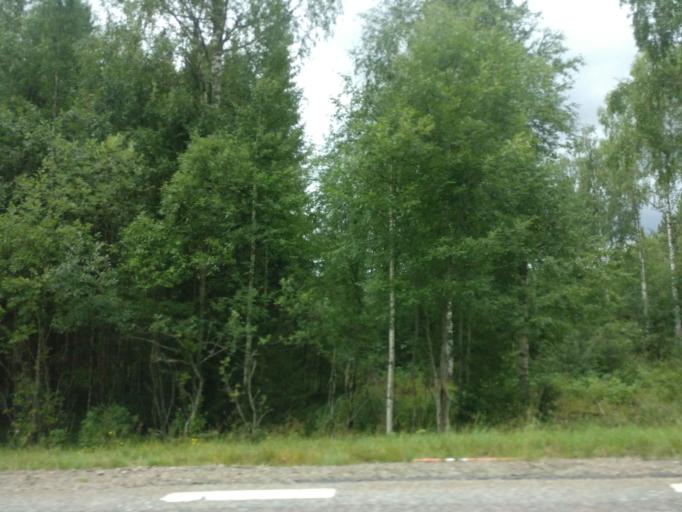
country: SE
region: Vaermland
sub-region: Torsby Kommun
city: Torsby
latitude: 60.7676
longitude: 12.7583
